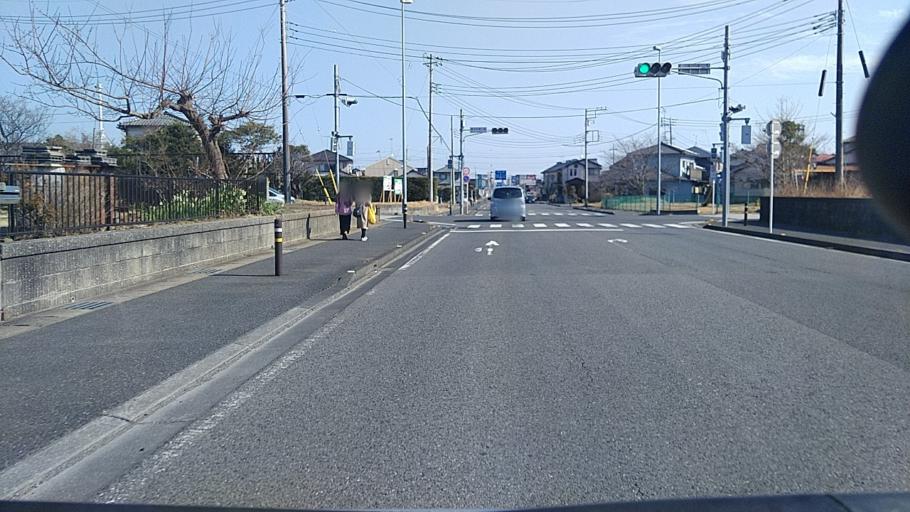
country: JP
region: Chiba
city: Mobara
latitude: 35.4250
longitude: 140.2824
